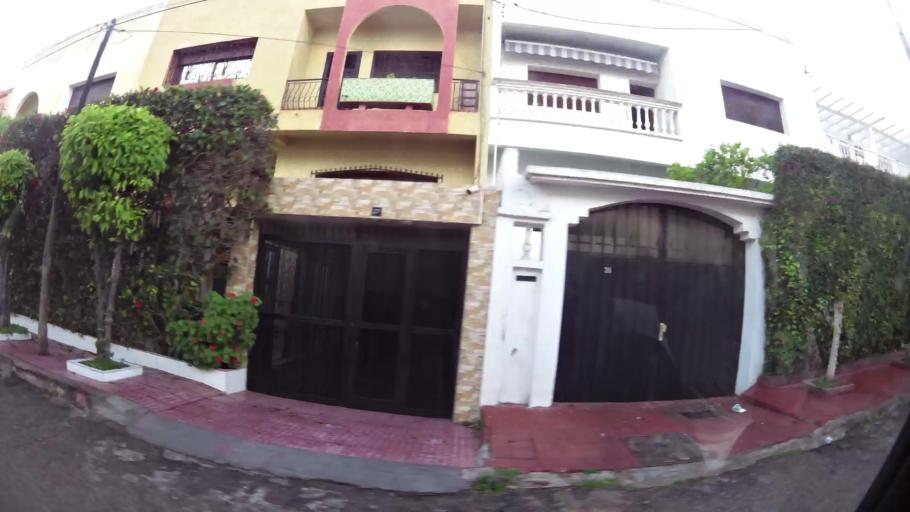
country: MA
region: Grand Casablanca
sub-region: Casablanca
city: Casablanca
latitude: 33.5607
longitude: -7.6760
